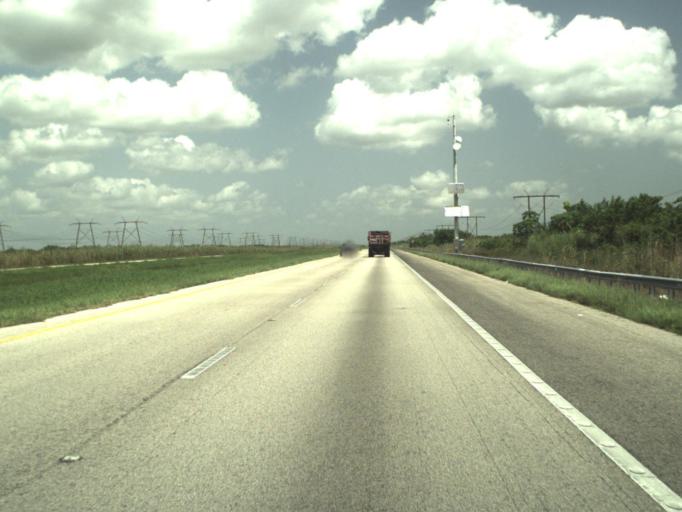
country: US
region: Florida
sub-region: Broward County
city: Weston
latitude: 26.2556
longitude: -80.4764
